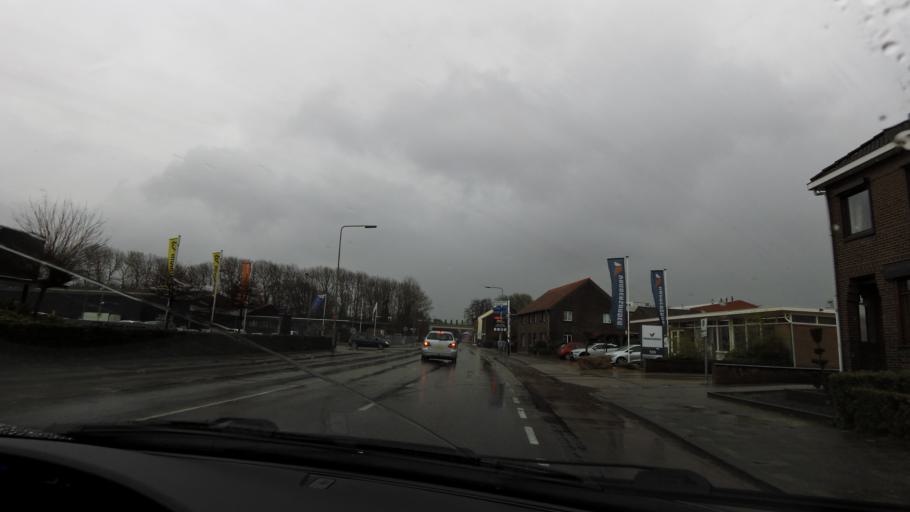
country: NL
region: Limburg
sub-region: Gemeente Beek
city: Beek
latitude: 50.9448
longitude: 5.7853
